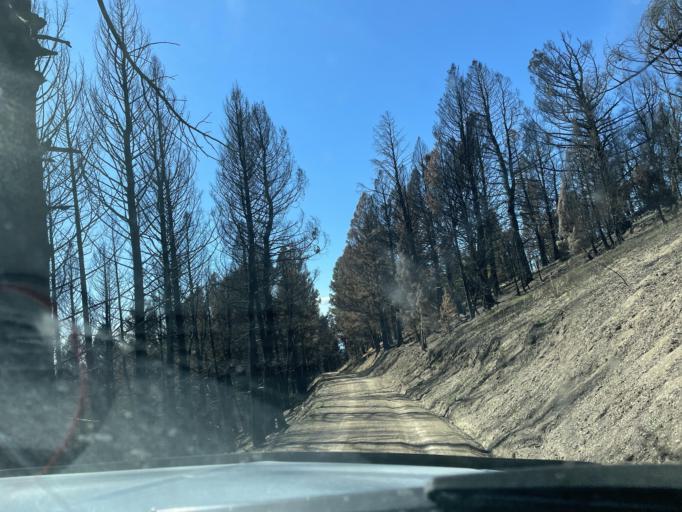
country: US
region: Montana
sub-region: Broadwater County
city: Townsend
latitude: 46.5071
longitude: -111.2807
